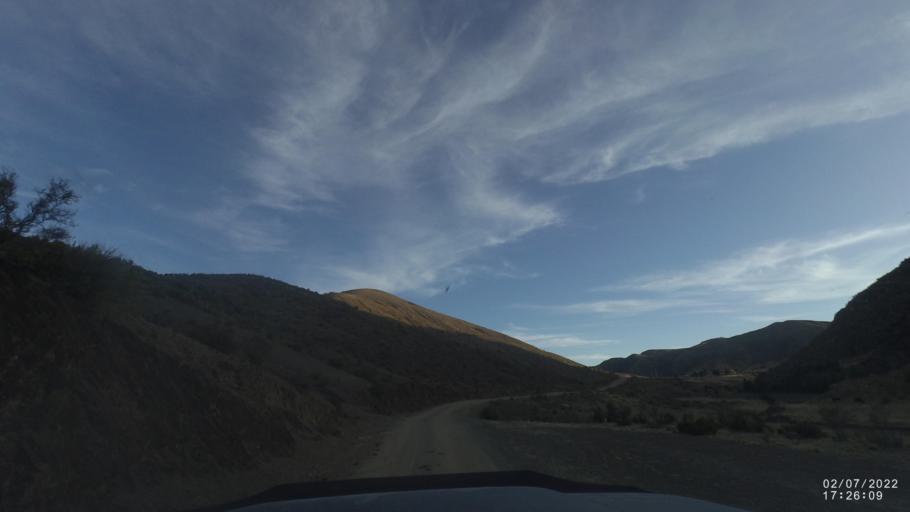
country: BO
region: Cochabamba
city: Irpa Irpa
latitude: -17.8789
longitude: -66.6095
